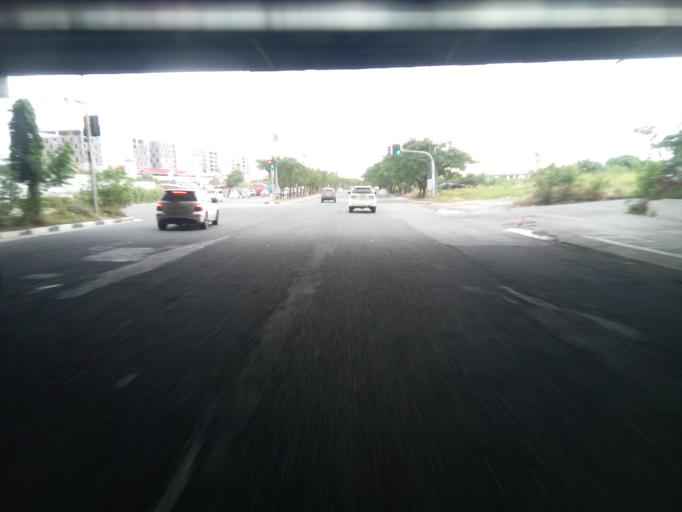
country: PH
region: Metro Manila
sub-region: Makati City
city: Makati City
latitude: 14.5153
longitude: 120.9901
